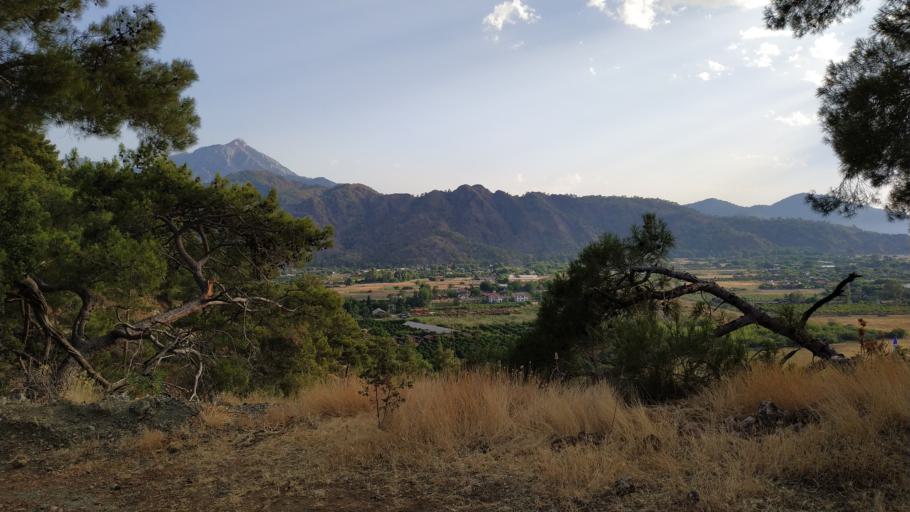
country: TR
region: Antalya
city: Tekirova
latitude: 36.4126
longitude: 30.4774
